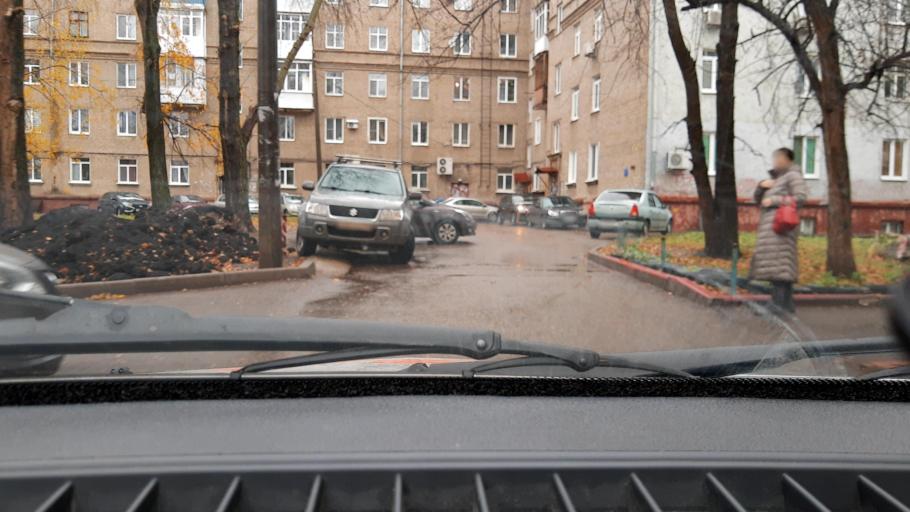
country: RU
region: Bashkortostan
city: Ufa
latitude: 54.8156
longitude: 56.0975
